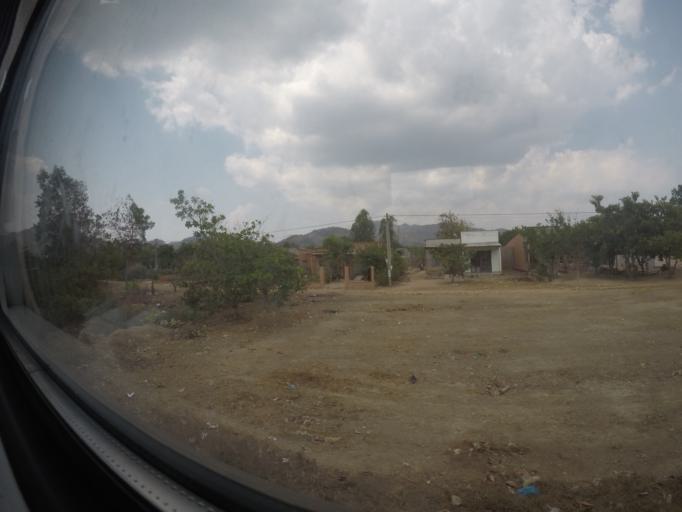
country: VN
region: Binh Thuan
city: Tanh Linh
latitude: 10.9595
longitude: 107.6448
